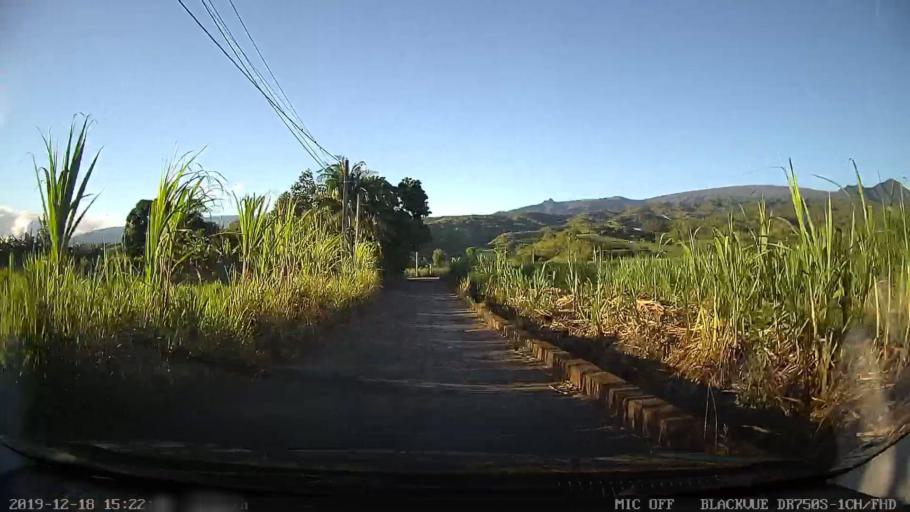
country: RE
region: Reunion
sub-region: Reunion
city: Bras-Panon
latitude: -20.9977
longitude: 55.6622
